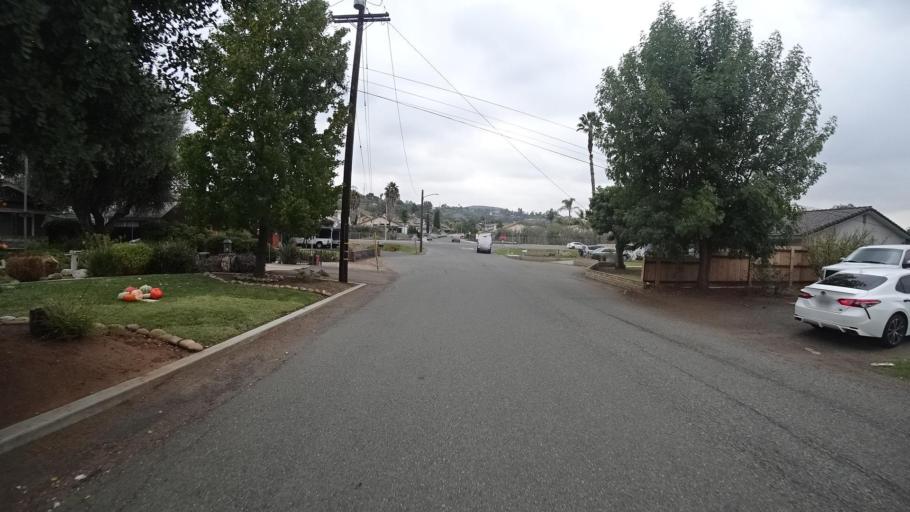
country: US
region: California
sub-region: San Diego County
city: Spring Valley
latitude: 32.7451
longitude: -116.9951
